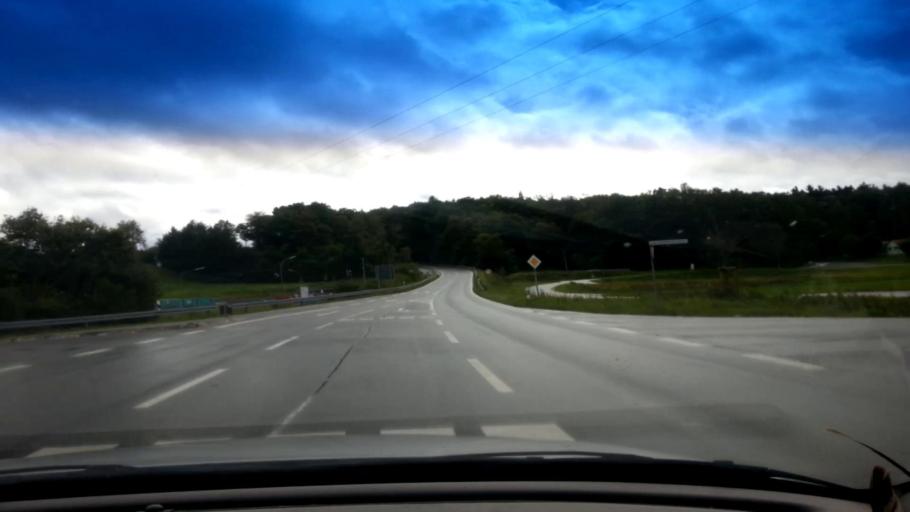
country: DE
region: Bavaria
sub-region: Upper Franconia
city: Frensdorf
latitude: 49.8501
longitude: 10.8812
